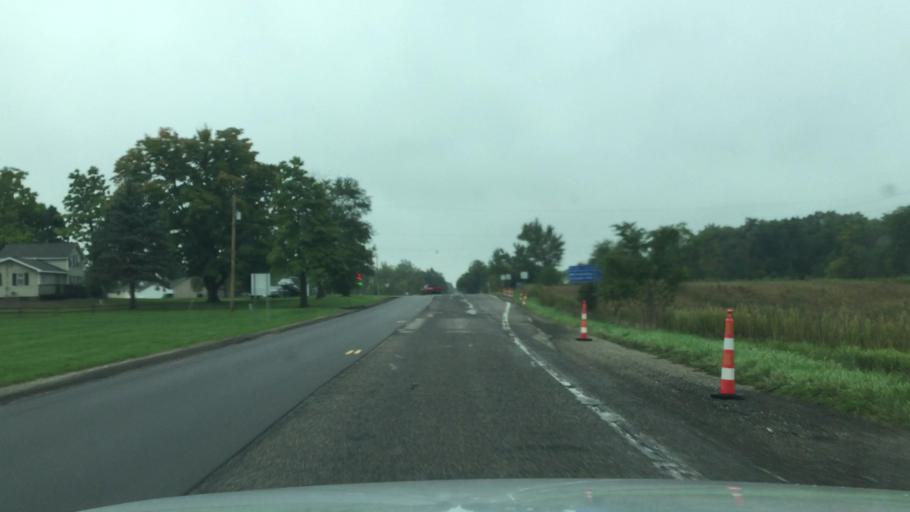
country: US
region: Michigan
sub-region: Shiawassee County
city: Perry
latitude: 42.9084
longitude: -84.2222
